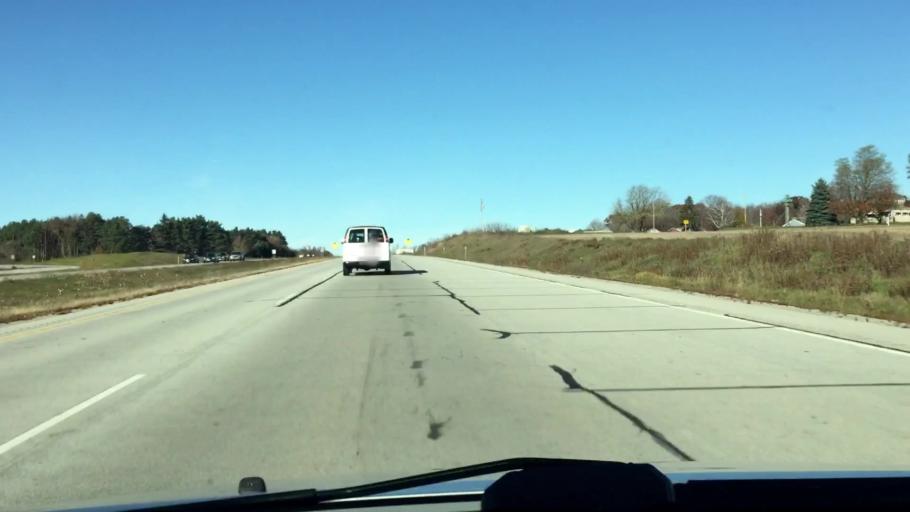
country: US
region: Wisconsin
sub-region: Brown County
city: Howard
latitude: 44.5636
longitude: -88.1377
